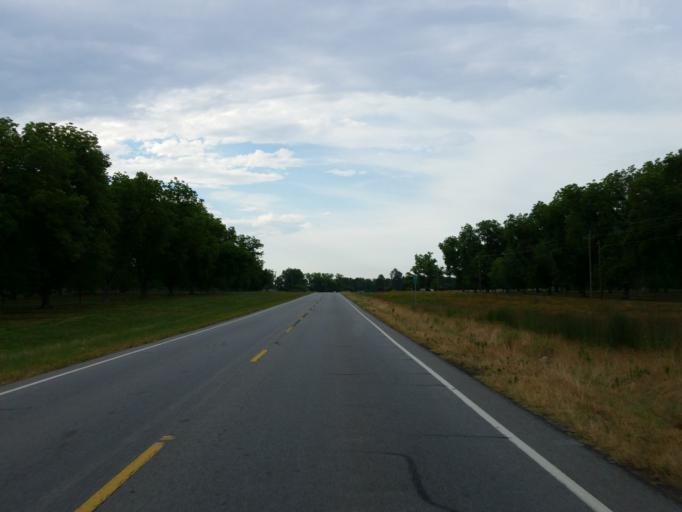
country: US
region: Georgia
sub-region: Dooly County
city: Vienna
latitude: 32.0432
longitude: -83.7952
